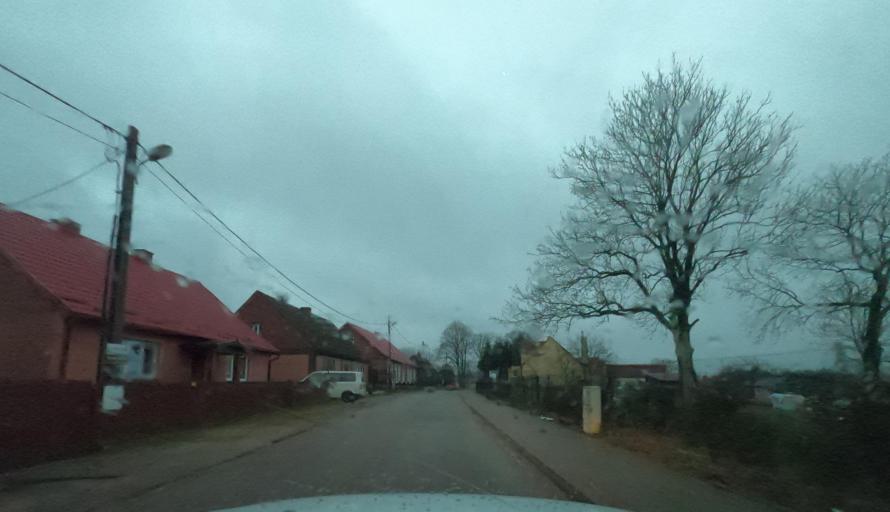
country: PL
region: West Pomeranian Voivodeship
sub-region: Powiat szczecinecki
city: Borne Sulinowo
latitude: 53.6711
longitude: 16.4903
